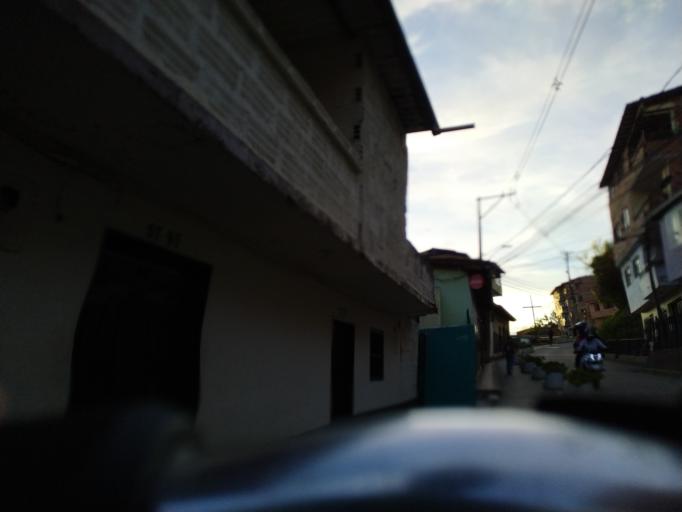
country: CO
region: Antioquia
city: Rionegro
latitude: 6.1582
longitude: -75.3760
